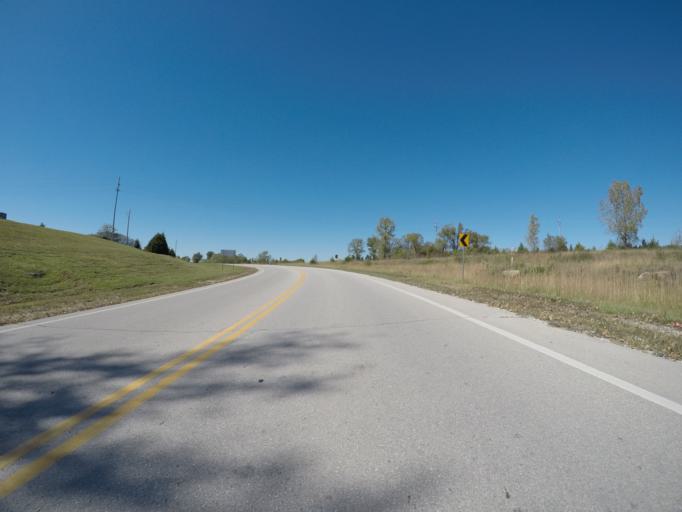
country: US
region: Kansas
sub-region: Douglas County
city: Eudora
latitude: 38.9420
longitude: -95.0738
